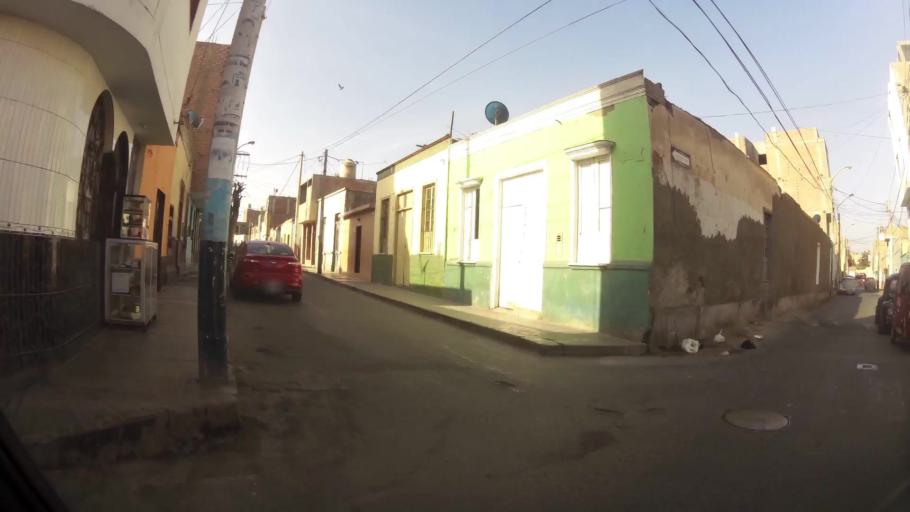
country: PE
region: Lima
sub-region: Huaura
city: Huacho
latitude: -11.1114
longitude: -77.6112
